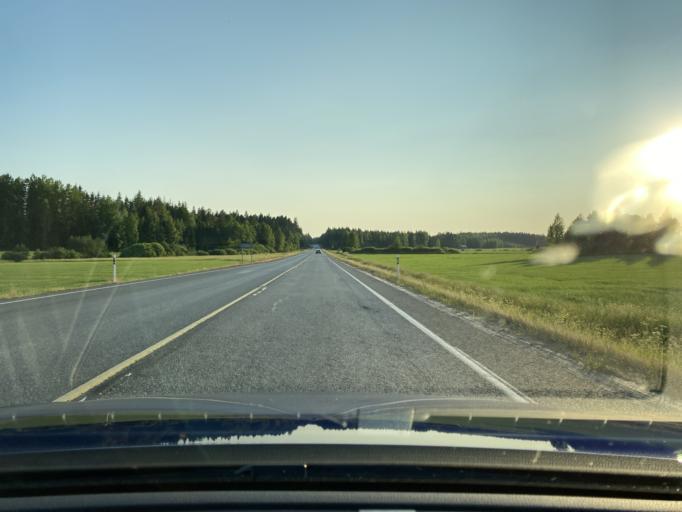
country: FI
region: Haeme
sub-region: Forssa
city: Forssa
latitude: 60.8302
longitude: 23.6922
